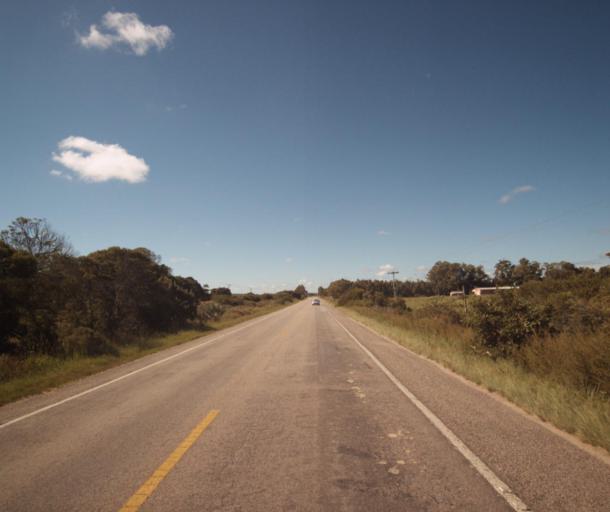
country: BR
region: Rio Grande do Sul
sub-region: Santa Vitoria Do Palmar
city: Santa Vitoria do Palmar
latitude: -33.5728
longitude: -53.3762
